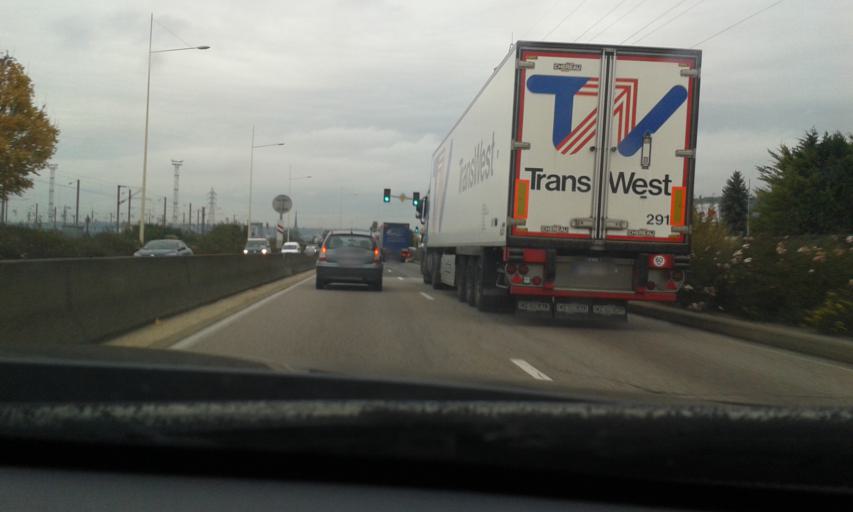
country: FR
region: Haute-Normandie
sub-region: Departement de la Seine-Maritime
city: Sotteville-les-Rouen
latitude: 49.4134
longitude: 1.1076
